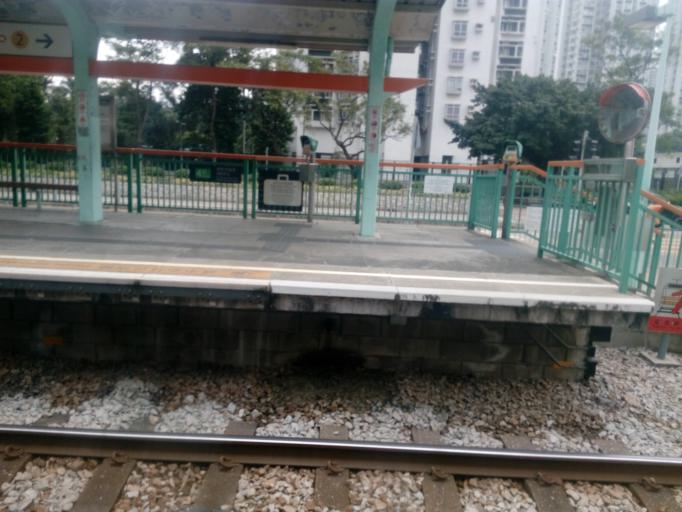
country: HK
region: Yuen Long
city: Yuen Long Kau Hui
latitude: 22.4596
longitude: 113.9993
